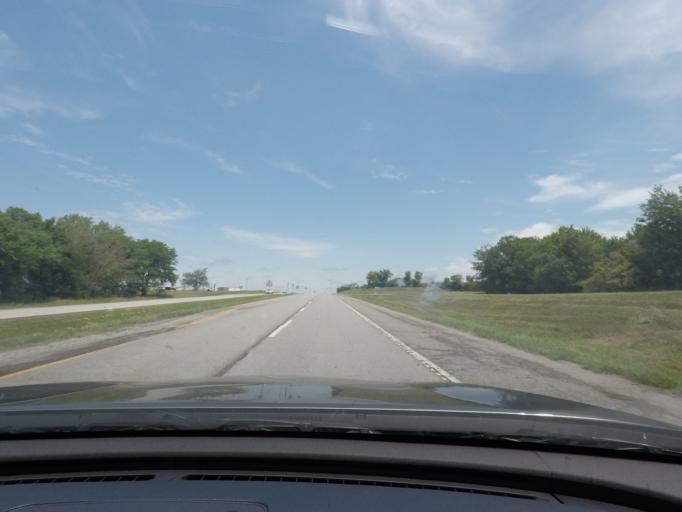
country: US
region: Missouri
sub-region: Saline County
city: Marshall
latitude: 39.0135
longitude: -93.1957
